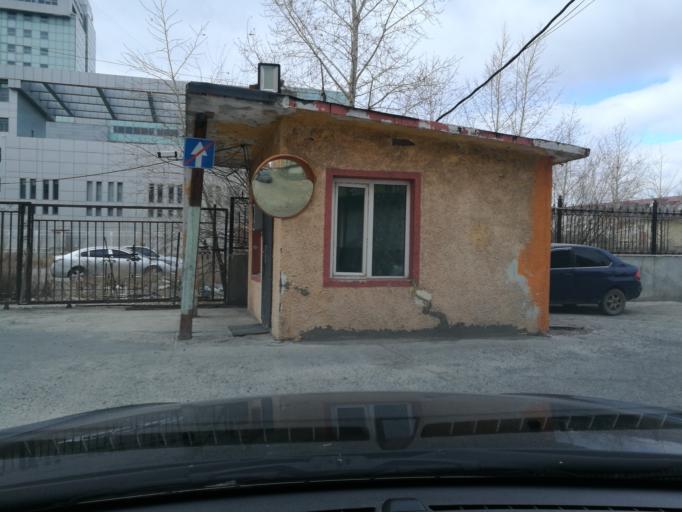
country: MN
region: Ulaanbaatar
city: Ulaanbaatar
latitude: 47.9041
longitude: 106.9244
